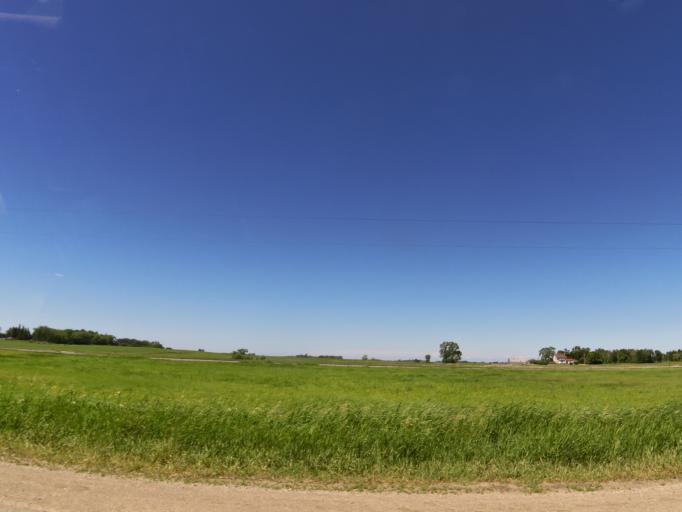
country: US
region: Minnesota
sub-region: Mahnomen County
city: Mahnomen
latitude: 47.0986
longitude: -95.9272
